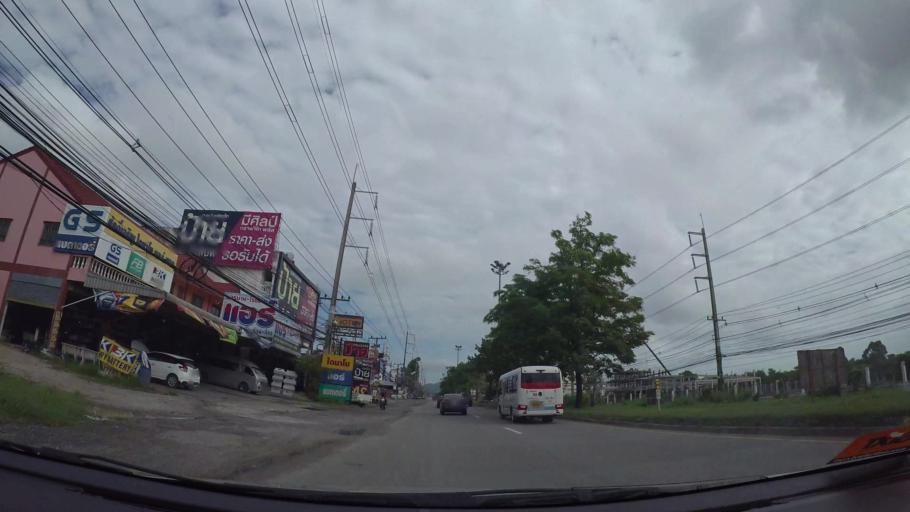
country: TH
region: Rayong
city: Rayong
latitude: 12.7084
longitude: 101.1766
